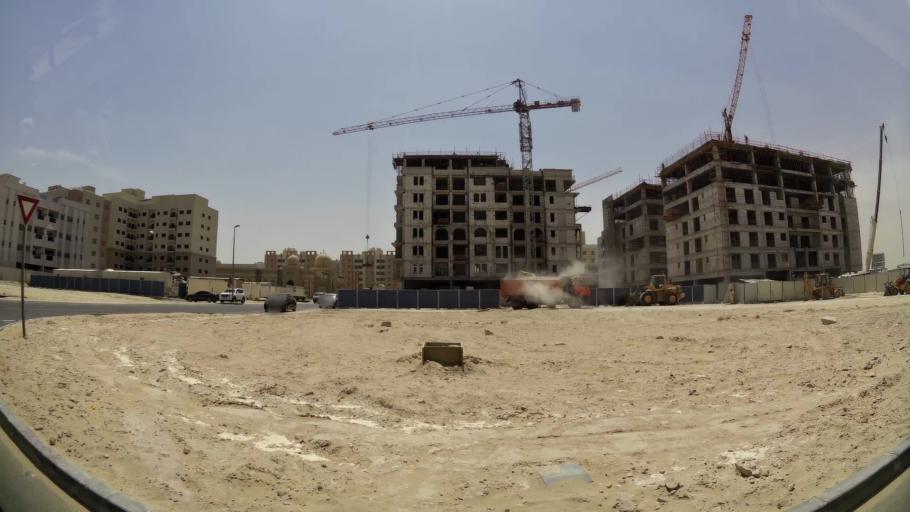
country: AE
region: Ash Shariqah
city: Sharjah
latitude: 25.1826
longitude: 55.4050
